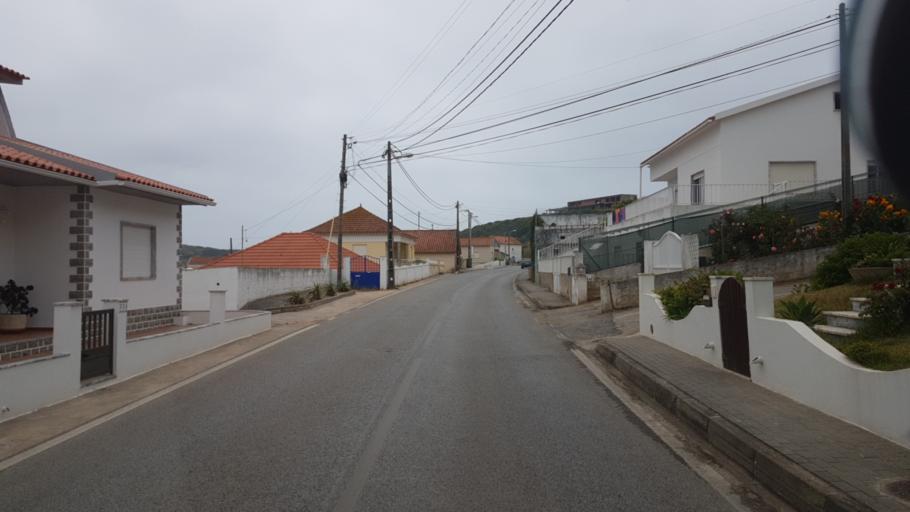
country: PT
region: Lisbon
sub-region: Torres Vedras
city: A dos Cunhados
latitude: 39.1807
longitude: -9.3361
